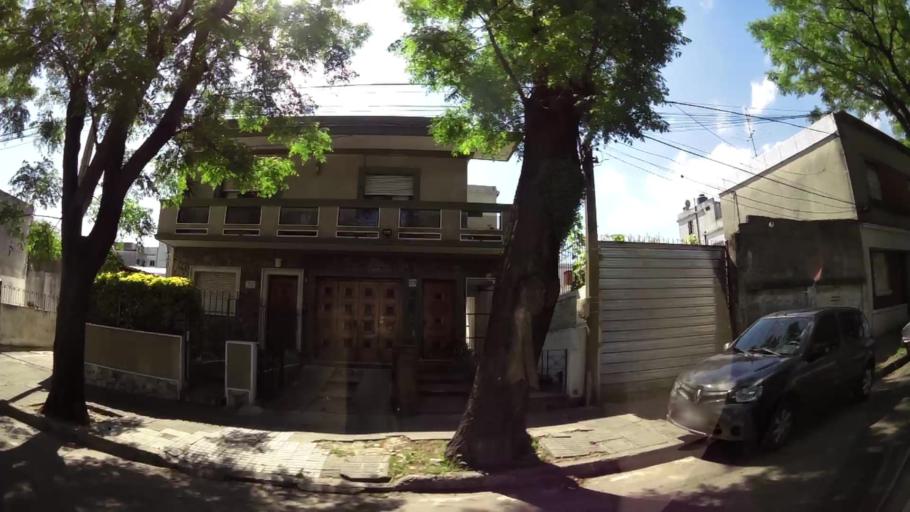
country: UY
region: Montevideo
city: Montevideo
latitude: -34.8591
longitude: -56.2250
